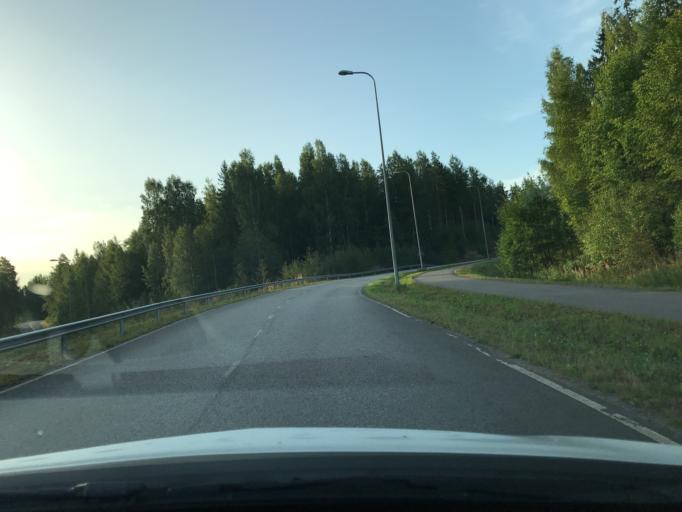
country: FI
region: Uusimaa
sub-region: Helsinki
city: Vihti
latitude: 60.4098
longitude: 24.4717
